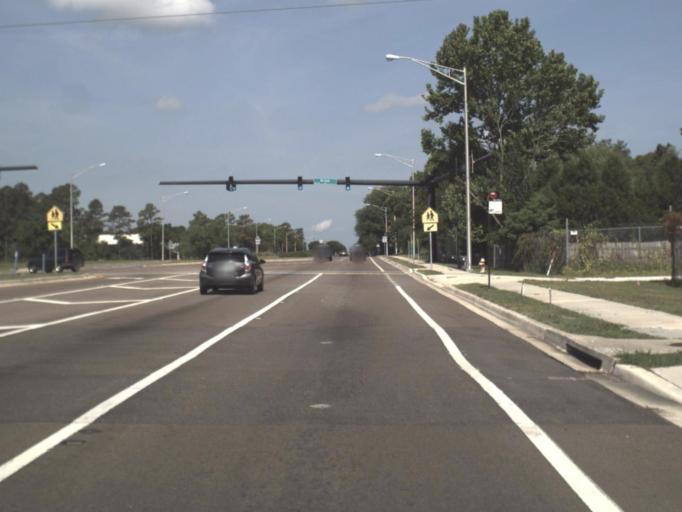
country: US
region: Florida
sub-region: Duval County
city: Atlantic Beach
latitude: 30.3597
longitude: -81.4894
